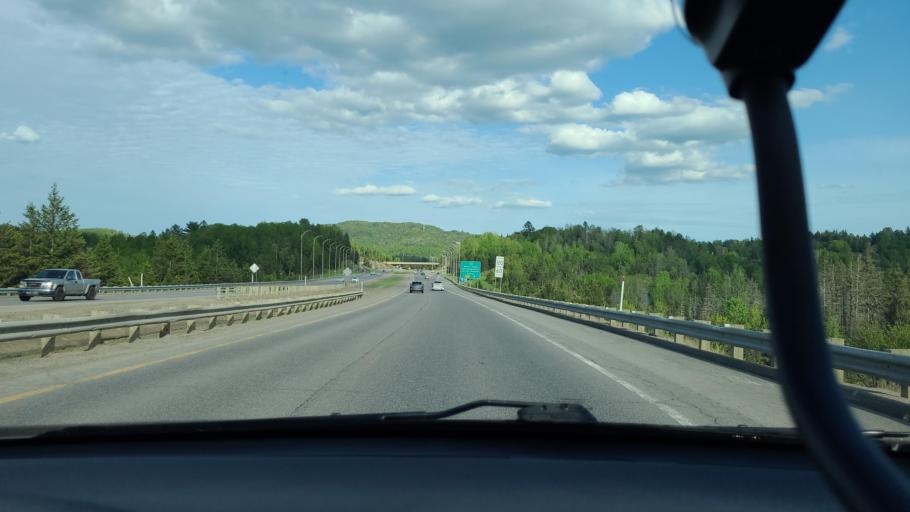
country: CA
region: Quebec
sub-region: Laurentides
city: Sainte-Adele
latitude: 45.9610
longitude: -74.1412
